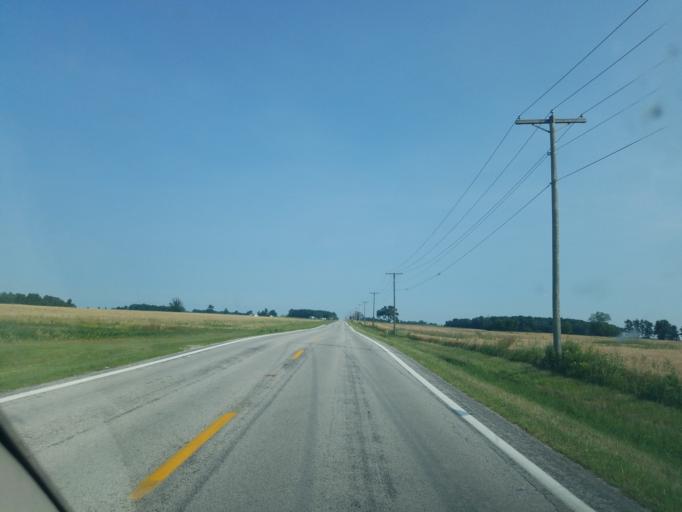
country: US
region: Ohio
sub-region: Wyandot County
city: Carey
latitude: 41.0250
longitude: -83.2947
